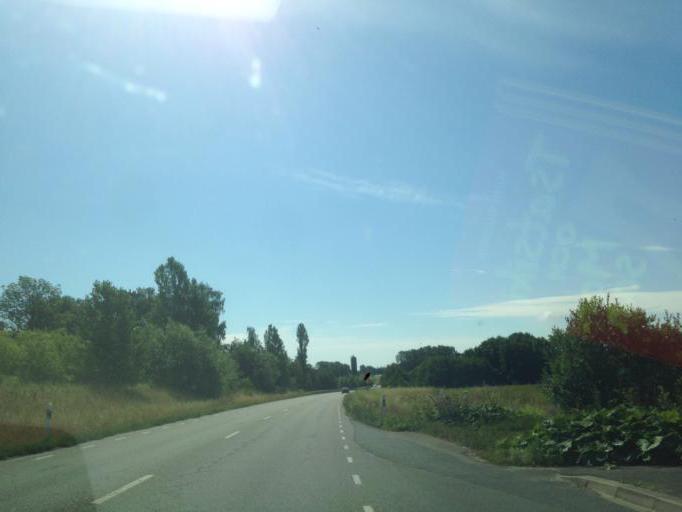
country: SE
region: Skane
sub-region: Simrishamns Kommun
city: Kivik
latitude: 55.6304
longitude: 14.2531
